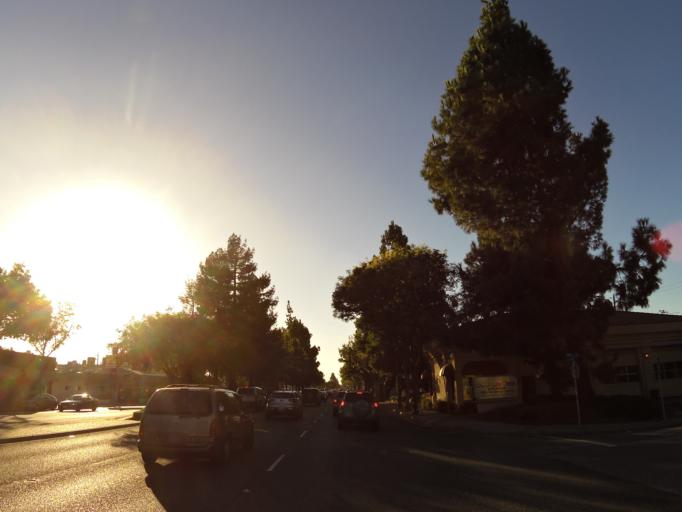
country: US
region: California
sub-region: Santa Clara County
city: Mountain View
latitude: 37.3842
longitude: -122.0806
